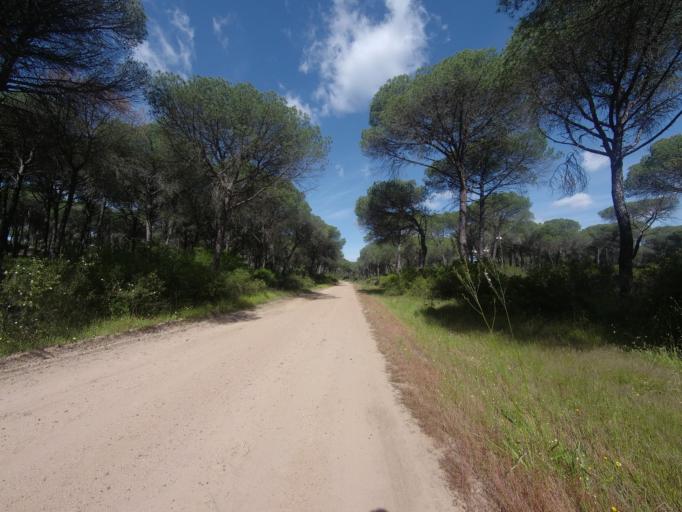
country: ES
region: Andalusia
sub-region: Provincia de Huelva
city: Aljaraque
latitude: 37.2357
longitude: -7.0537
